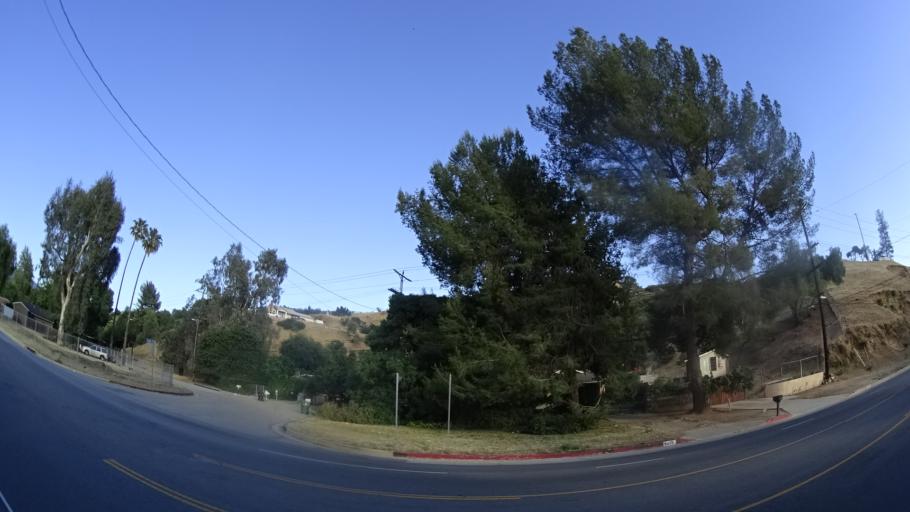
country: US
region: California
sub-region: Los Angeles County
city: North Hollywood
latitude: 34.2461
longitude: -118.3622
